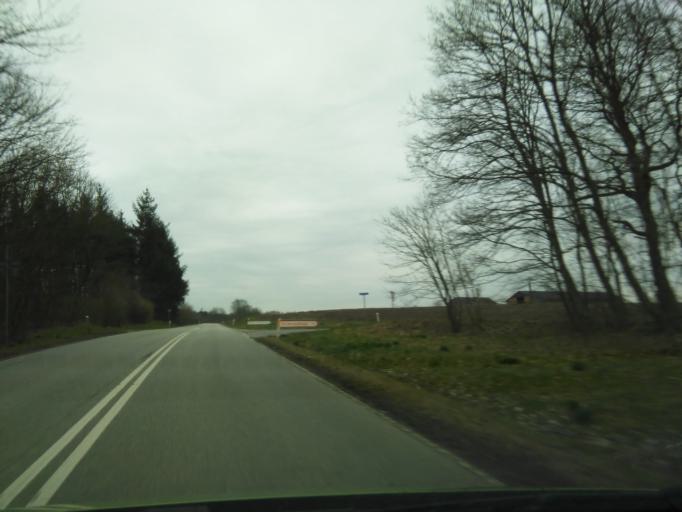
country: DK
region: North Denmark
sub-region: Mariagerfjord Kommune
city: Mariager
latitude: 56.5972
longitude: 9.9985
